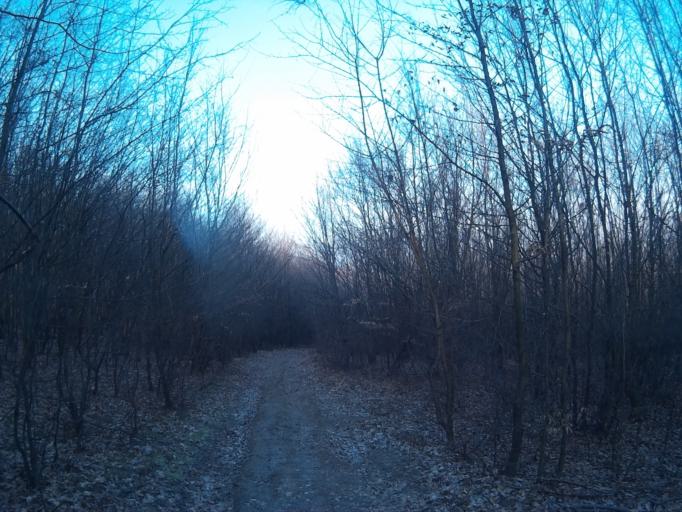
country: HU
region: Nograd
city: Bercel
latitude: 47.9134
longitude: 19.4167
